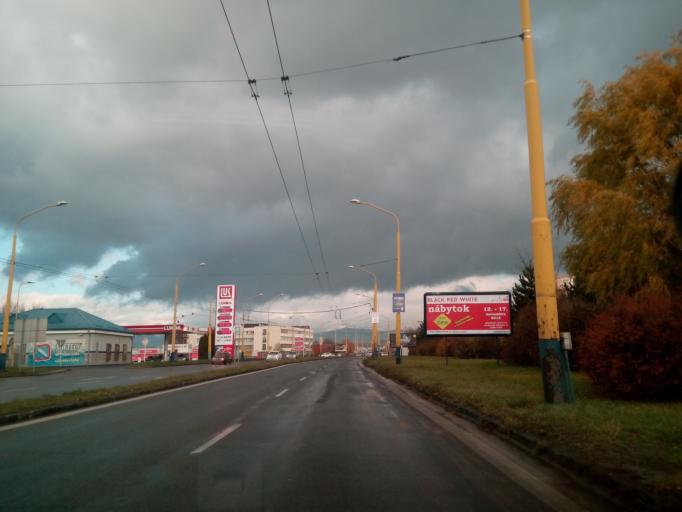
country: SK
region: Presovsky
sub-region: Okres Presov
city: Presov
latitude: 48.9913
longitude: 21.2661
